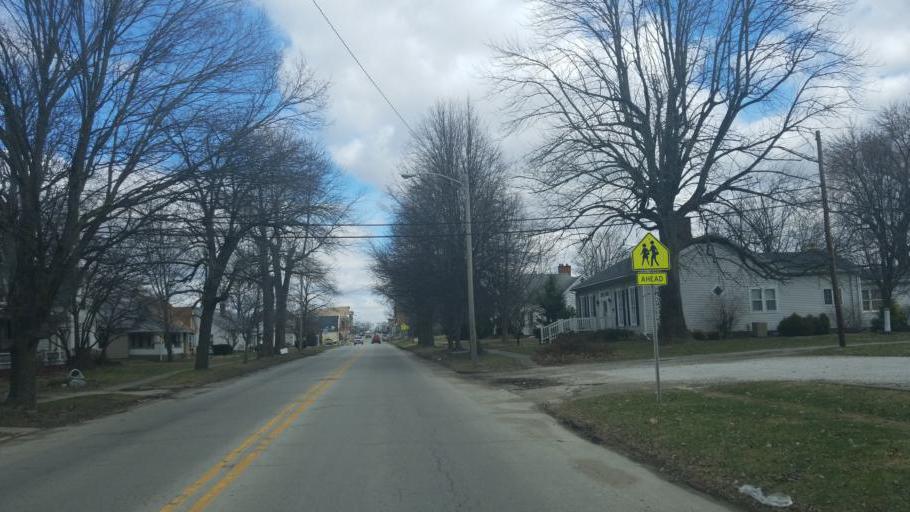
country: US
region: Indiana
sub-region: Parke County
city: Rockville
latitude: 39.7625
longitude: -87.2332
